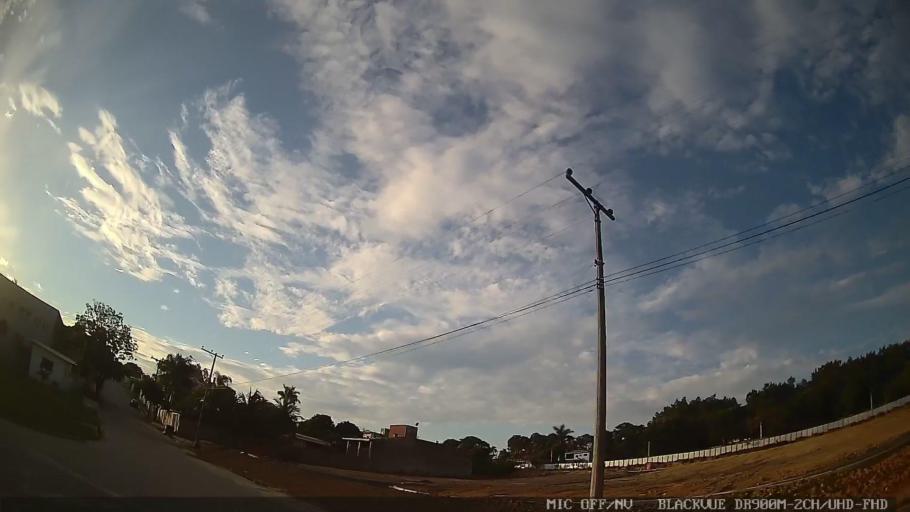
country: BR
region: Sao Paulo
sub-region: Salto
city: Salto
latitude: -23.1970
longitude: -47.2796
